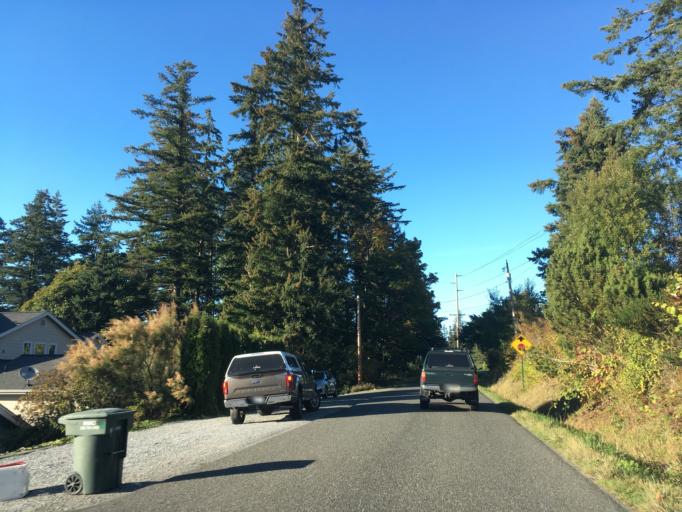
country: US
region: Washington
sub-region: Whatcom County
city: Bellingham
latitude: 48.7178
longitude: -122.4698
